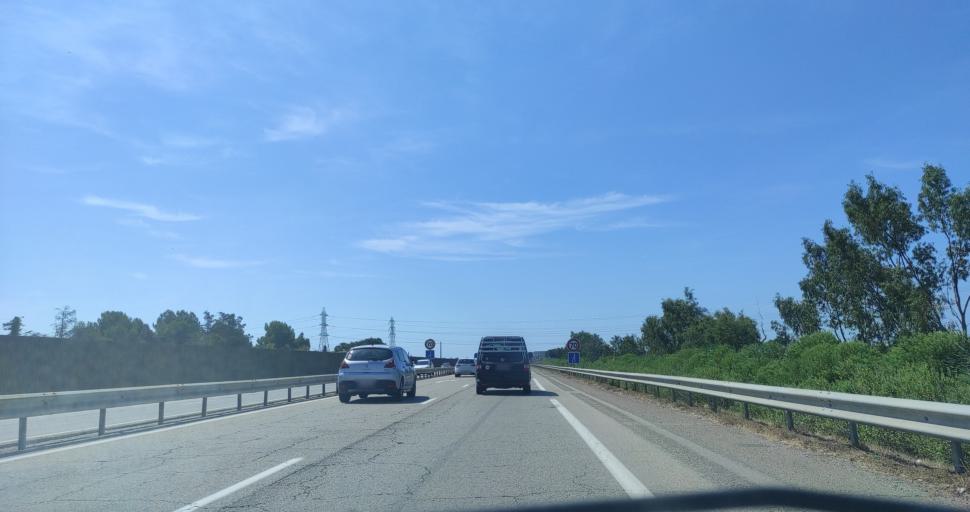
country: FR
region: Provence-Alpes-Cote d'Azur
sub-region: Departement des Bouches-du-Rhone
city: Fos-sur-Mer
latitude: 43.4373
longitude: 4.9408
